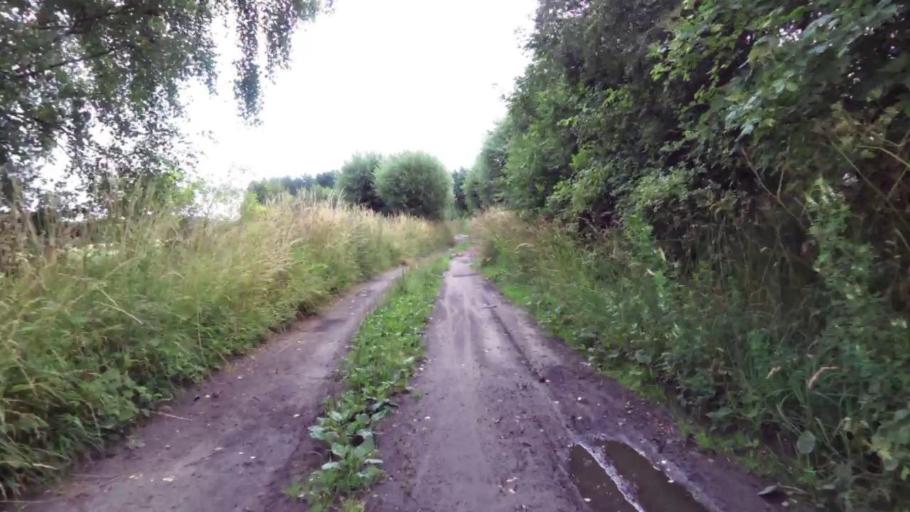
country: PL
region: West Pomeranian Voivodeship
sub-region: Powiat mysliborski
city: Mysliborz
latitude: 52.9648
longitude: 14.8946
